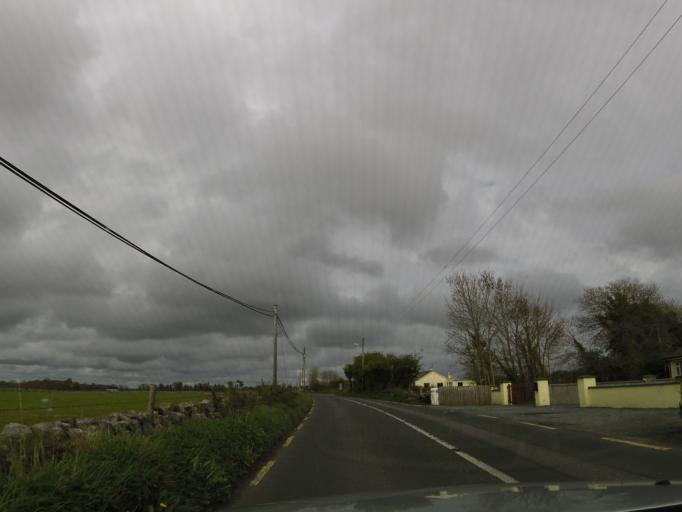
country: IE
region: Connaught
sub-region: Maigh Eo
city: Ballinrobe
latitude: 53.6286
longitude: -9.2079
